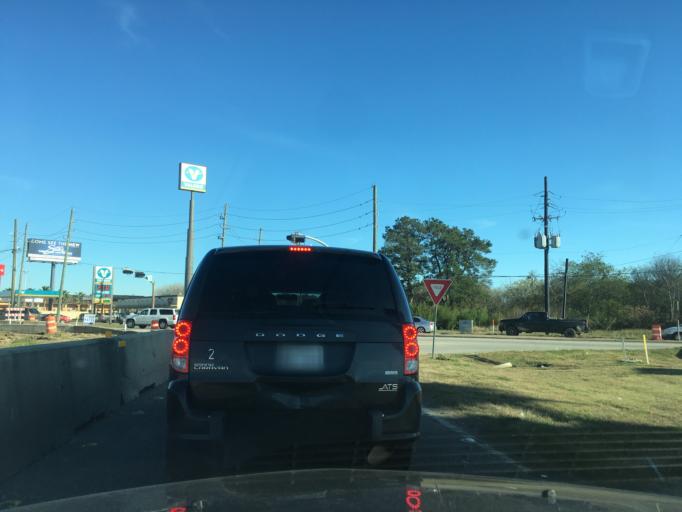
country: US
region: Texas
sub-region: Fort Bend County
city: Rosenberg
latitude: 29.5335
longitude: -95.7775
